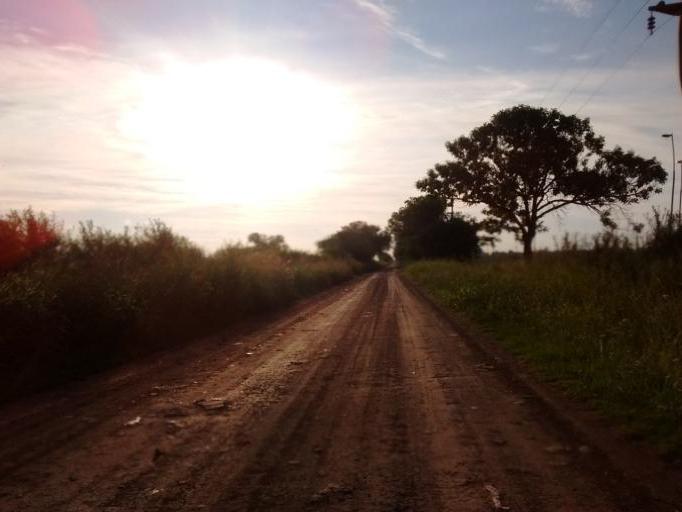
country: AR
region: Santa Fe
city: Funes
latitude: -32.9305
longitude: -60.8528
